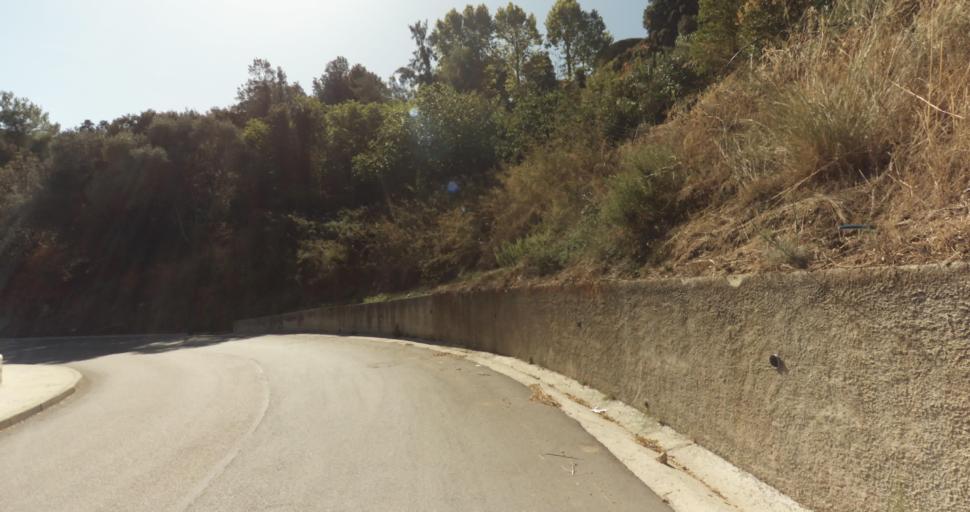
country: FR
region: Corsica
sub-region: Departement de la Corse-du-Sud
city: Ajaccio
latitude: 41.9252
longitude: 8.7148
